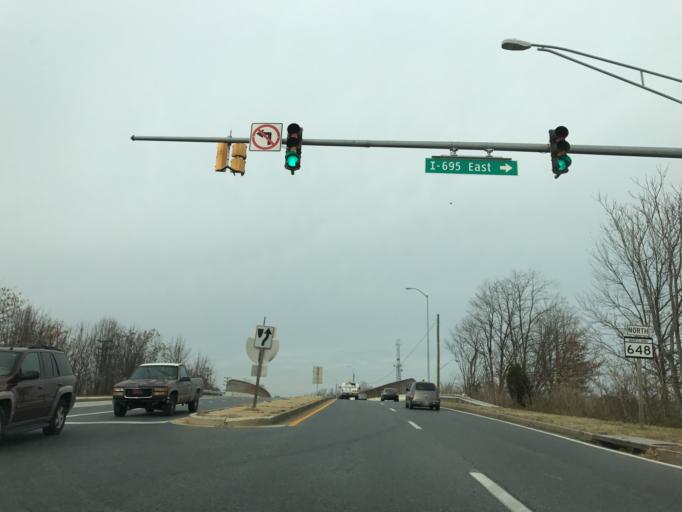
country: US
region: Maryland
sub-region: Anne Arundel County
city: Linthicum
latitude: 39.2048
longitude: -76.6416
